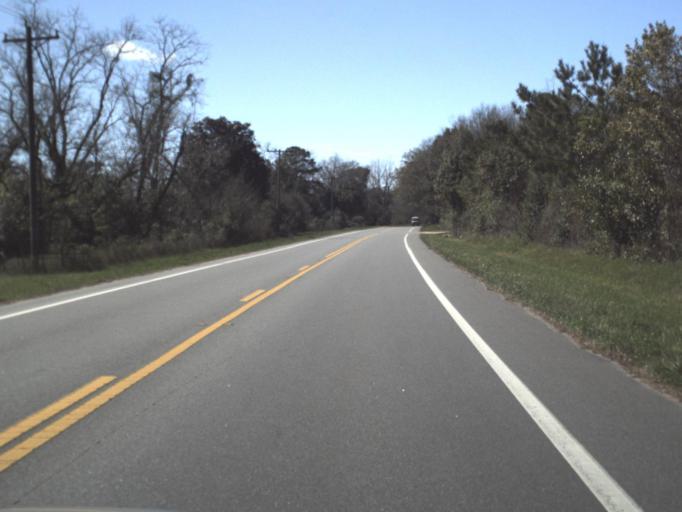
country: US
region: Florida
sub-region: Gadsden County
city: Chattahoochee
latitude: 30.6925
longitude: -84.7488
